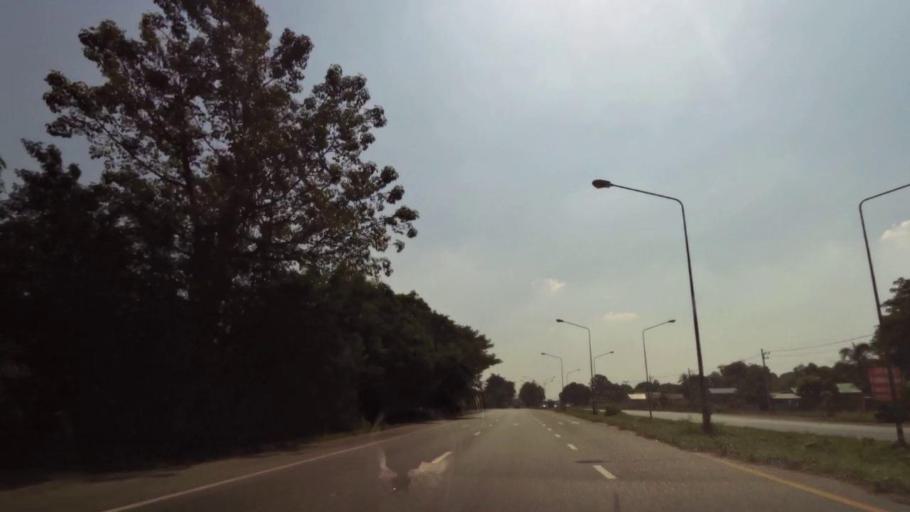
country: TH
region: Phichit
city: Bueng Na Rang
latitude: 16.1948
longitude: 100.1284
